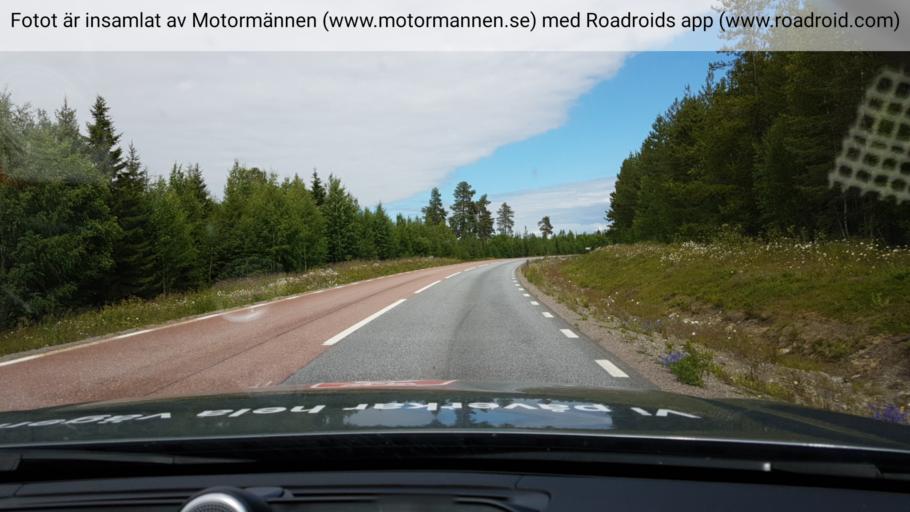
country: SE
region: Vaesterbotten
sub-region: Dorotea Kommun
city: Dorotea
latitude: 64.1402
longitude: 16.2230
